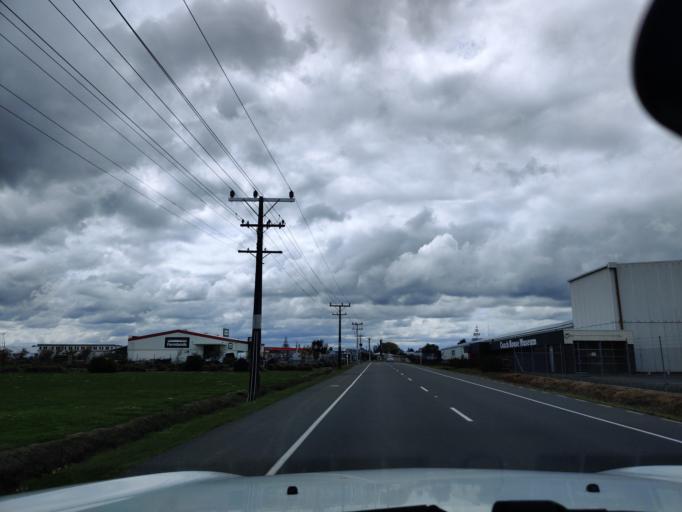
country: NZ
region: Manawatu-Wanganui
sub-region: Palmerston North City
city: Palmerston North
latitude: -40.2323
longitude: 175.5664
